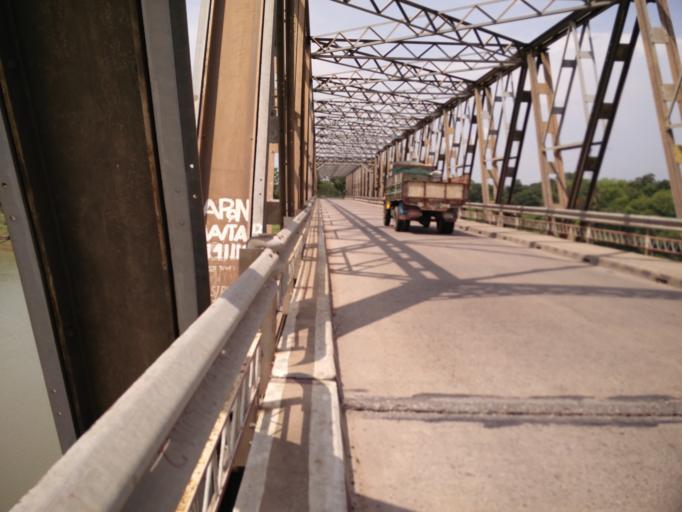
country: BD
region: Khulna
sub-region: Magura
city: Magura
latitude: 23.5433
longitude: 89.5177
